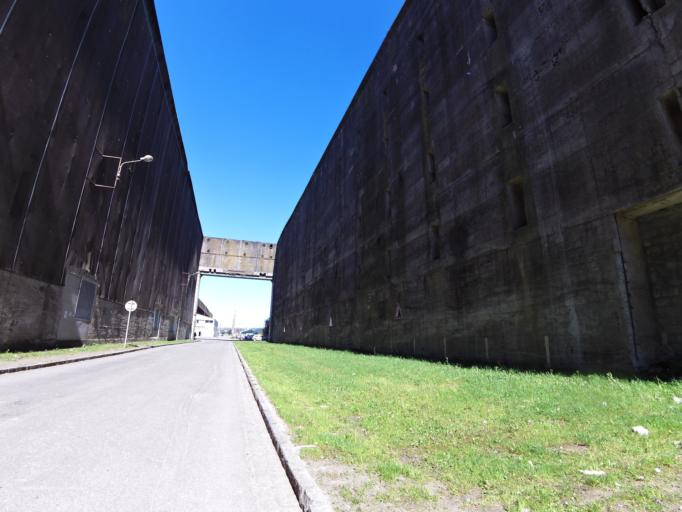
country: FR
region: Brittany
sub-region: Departement du Morbihan
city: Lorient
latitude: 47.7295
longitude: -3.3695
